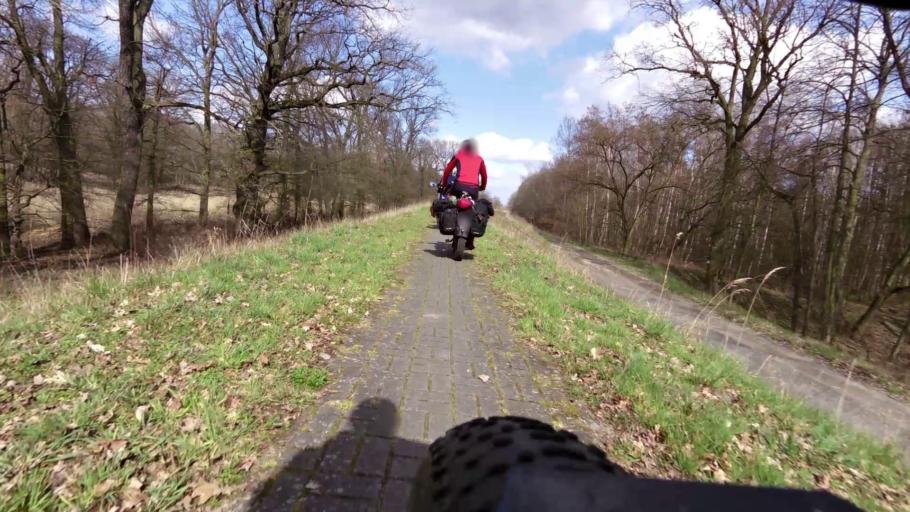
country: DE
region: Brandenburg
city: Lebus
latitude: 52.3962
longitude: 14.5409
